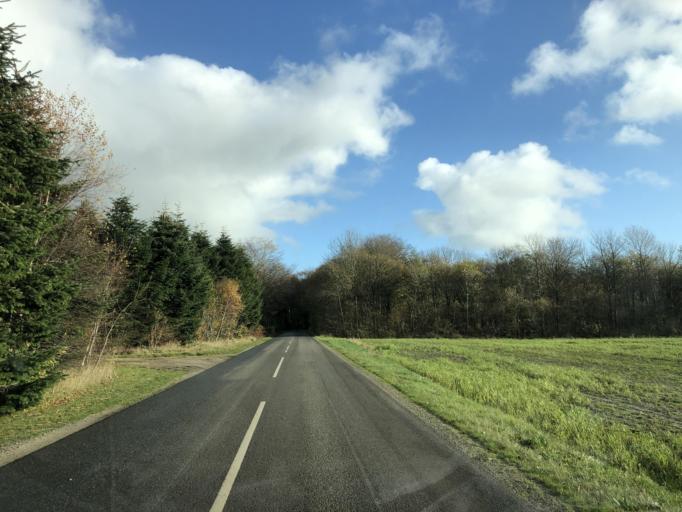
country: DK
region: Central Jutland
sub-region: Ringkobing-Skjern Kommune
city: Ringkobing
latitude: 56.1382
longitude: 8.3516
